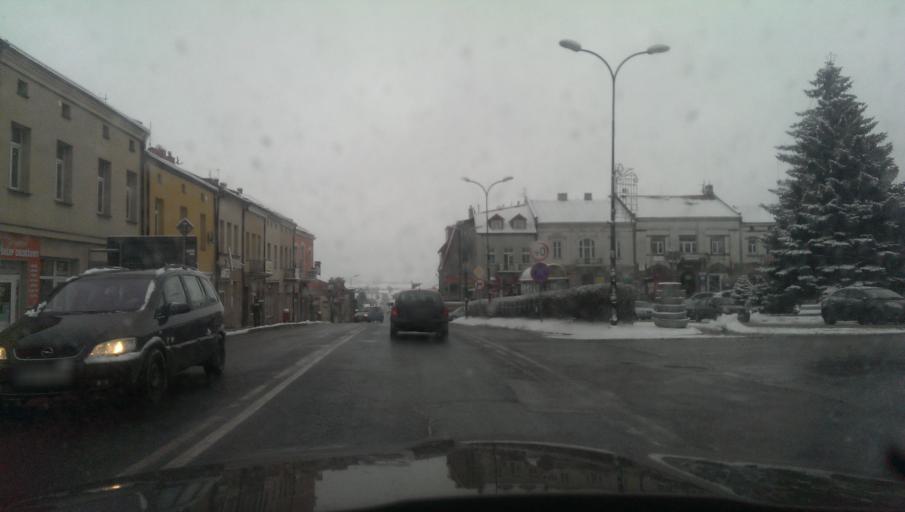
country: PL
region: Subcarpathian Voivodeship
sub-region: Powiat krosnienski
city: Rymanow
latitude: 49.5766
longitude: 21.8672
